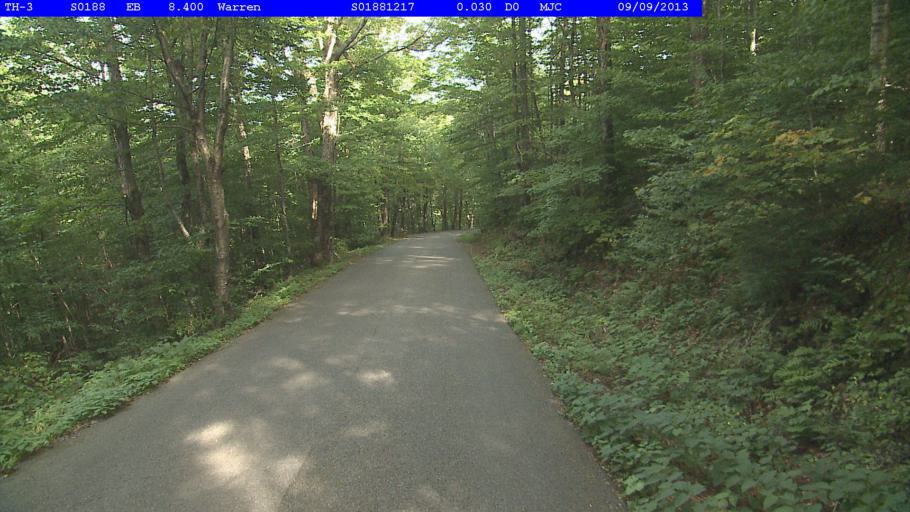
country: US
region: Vermont
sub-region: Addison County
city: Bristol
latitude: 44.0949
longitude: -72.9217
